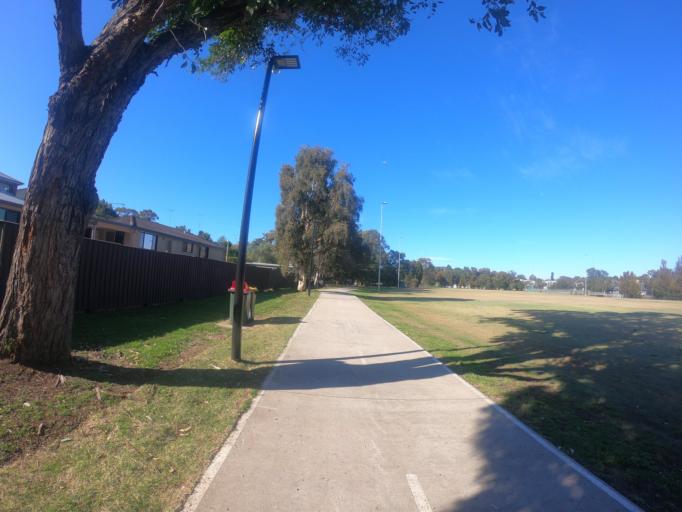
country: AU
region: New South Wales
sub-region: Hunters Hill
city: Gladesville
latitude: -33.8277
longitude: 151.1148
